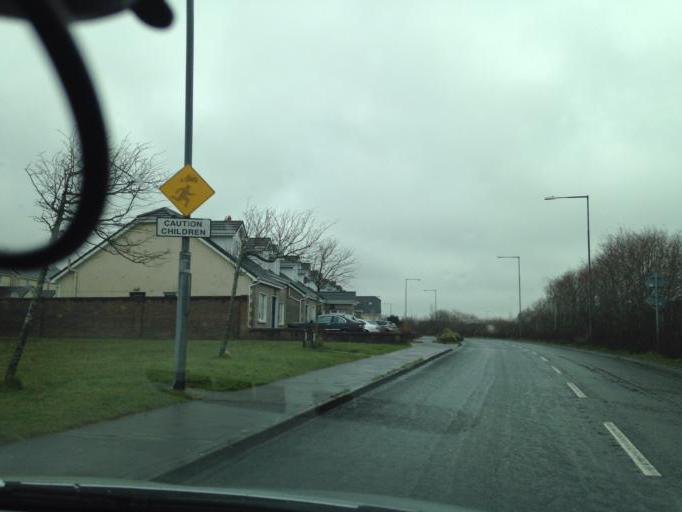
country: IE
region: Connaught
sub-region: County Galway
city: Gaillimh
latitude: 53.2749
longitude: -9.0985
